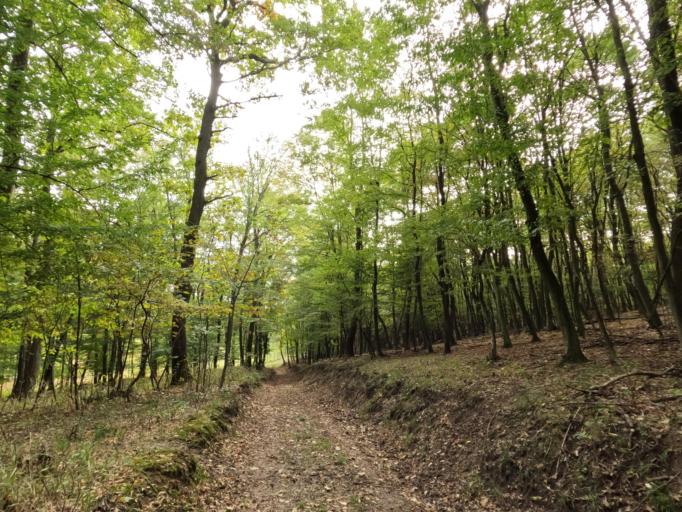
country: HU
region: Tolna
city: Szentgalpuszta
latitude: 46.3132
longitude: 18.6434
